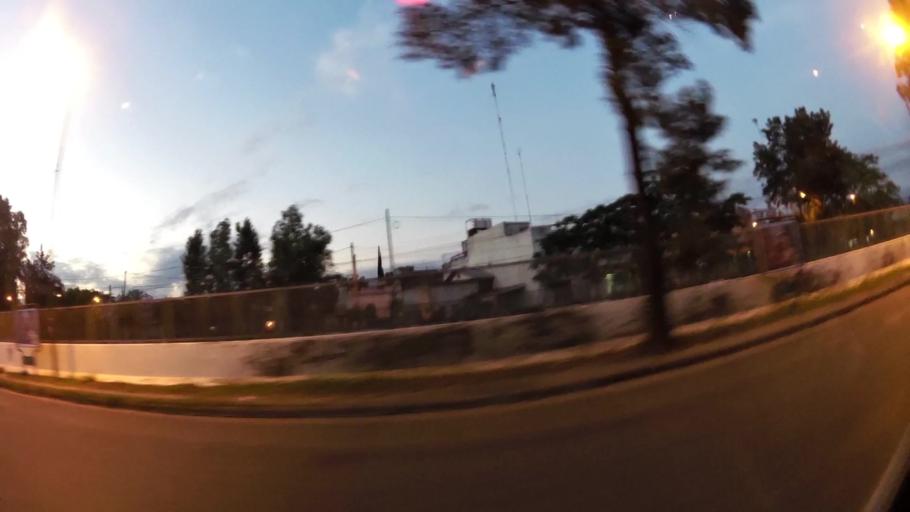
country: AR
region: Buenos Aires
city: Ituzaingo
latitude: -34.6614
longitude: -58.6714
